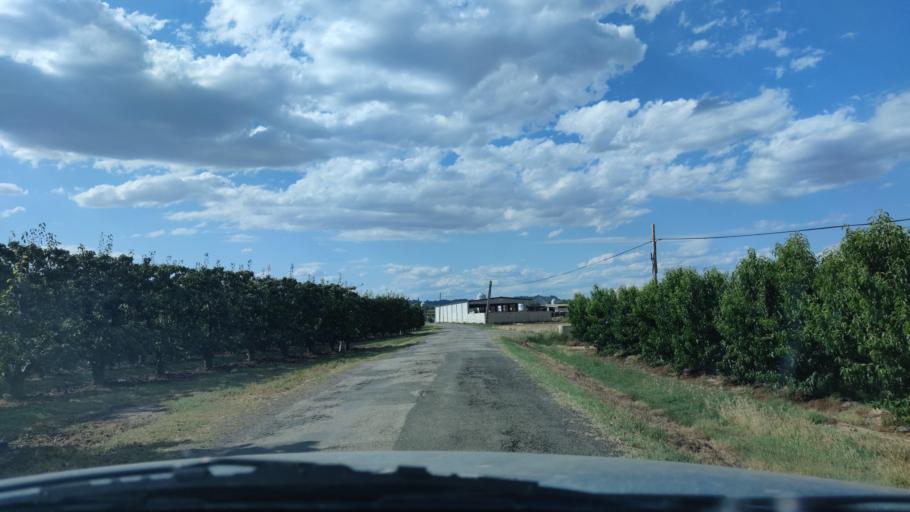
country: ES
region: Catalonia
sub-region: Provincia de Lleida
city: Alcarras
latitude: 41.5968
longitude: 0.5300
